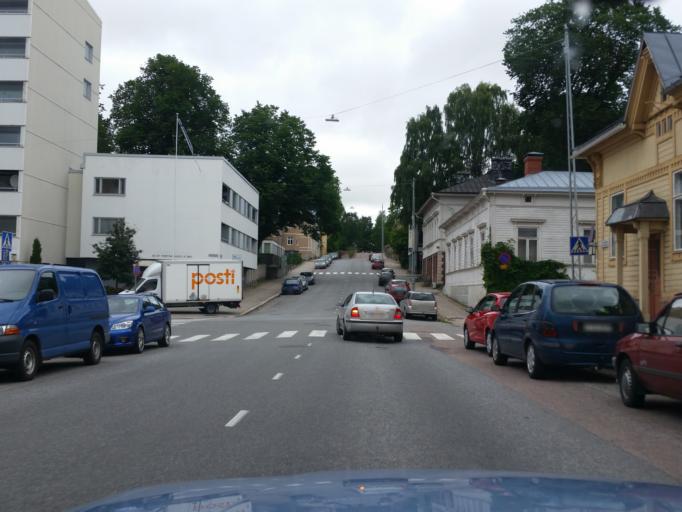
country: FI
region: Varsinais-Suomi
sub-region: Turku
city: Turku
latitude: 60.4535
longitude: 22.2808
